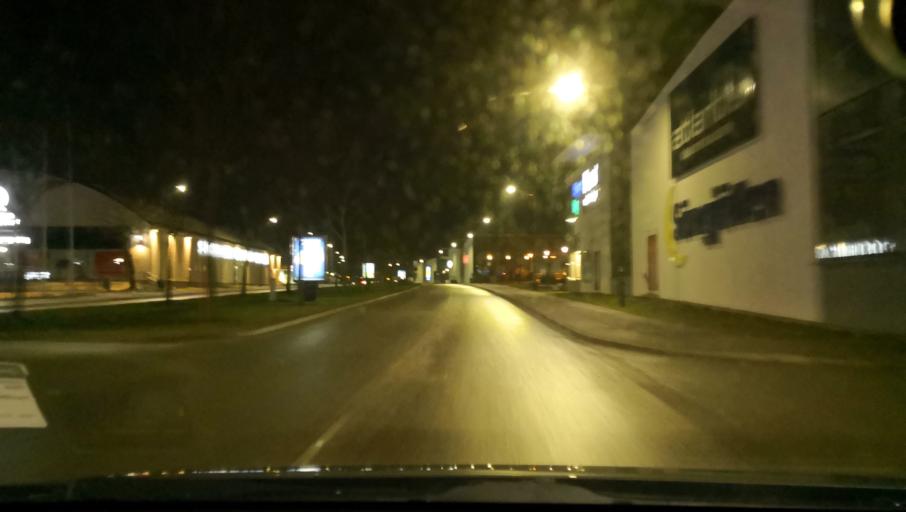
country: SE
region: Stockholm
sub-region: Jarfalla Kommun
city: Jakobsberg
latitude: 59.4167
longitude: 17.8604
